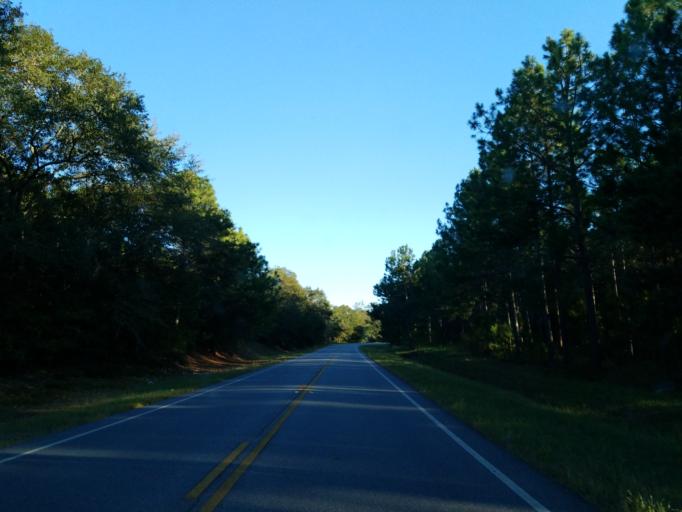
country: US
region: Georgia
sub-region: Worth County
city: Sylvester
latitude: 31.5788
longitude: -83.8563
